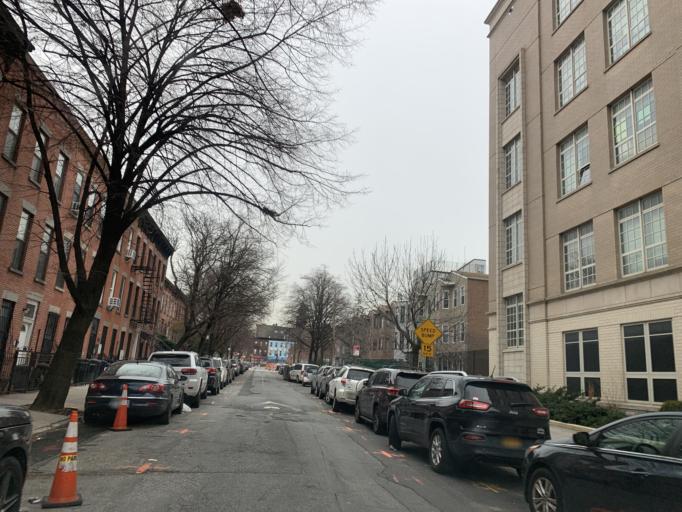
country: US
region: New York
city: New York City
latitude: 40.6804
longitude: -73.9805
